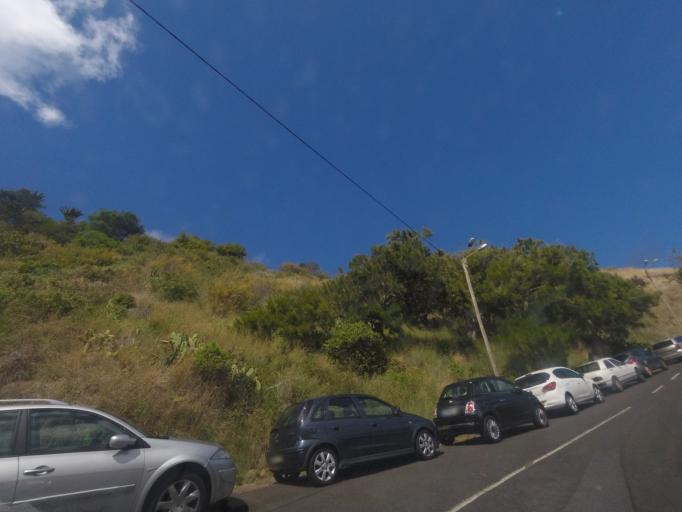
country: PT
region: Madeira
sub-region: Machico
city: Canical
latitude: 32.7361
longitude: -16.7463
